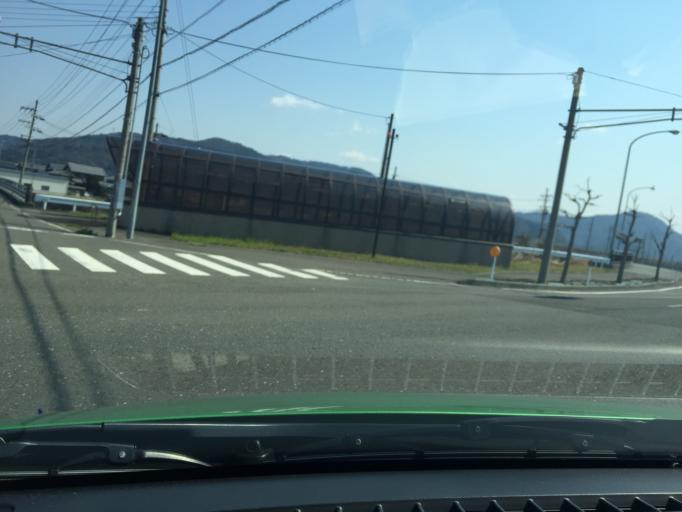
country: JP
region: Fukui
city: Obama
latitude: 35.4931
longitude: 135.7606
